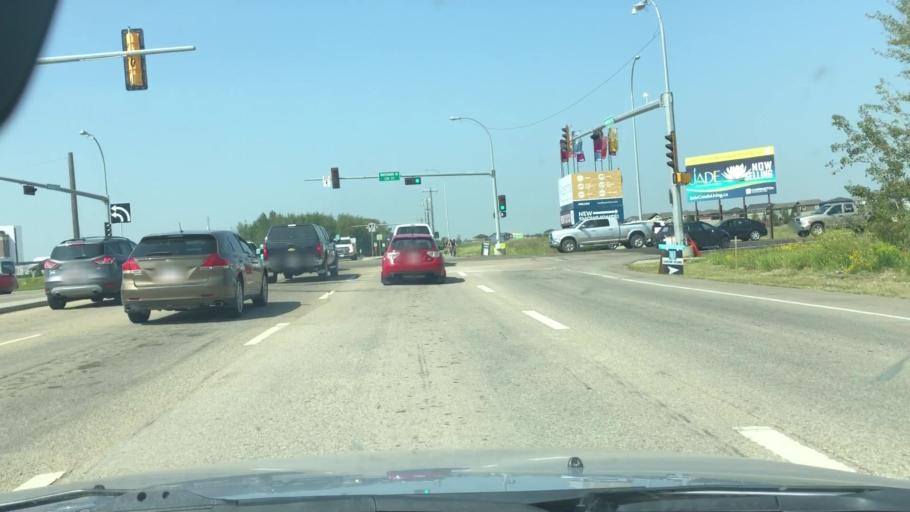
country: CA
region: Alberta
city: St. Albert
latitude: 53.5123
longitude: -113.6881
